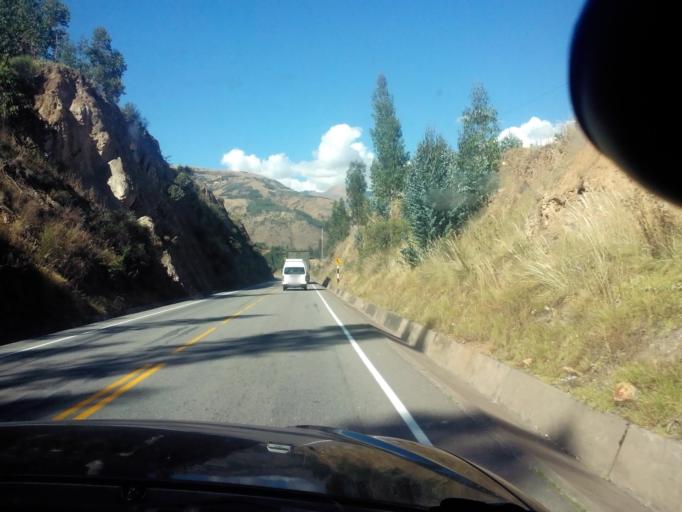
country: PE
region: Cusco
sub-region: Provincia de Quispicanchis
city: Urcos
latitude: -13.6957
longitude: -71.5984
